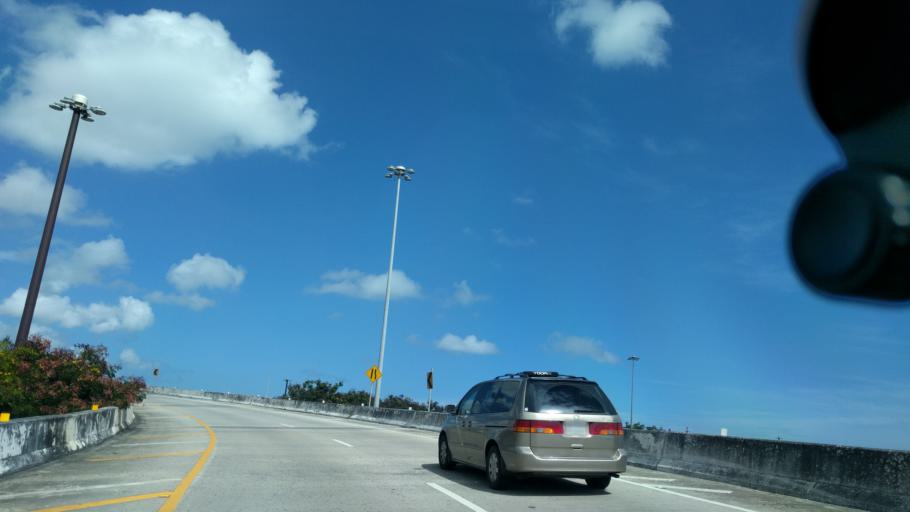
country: PR
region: Catano
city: Catano
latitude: 18.4284
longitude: -66.0741
